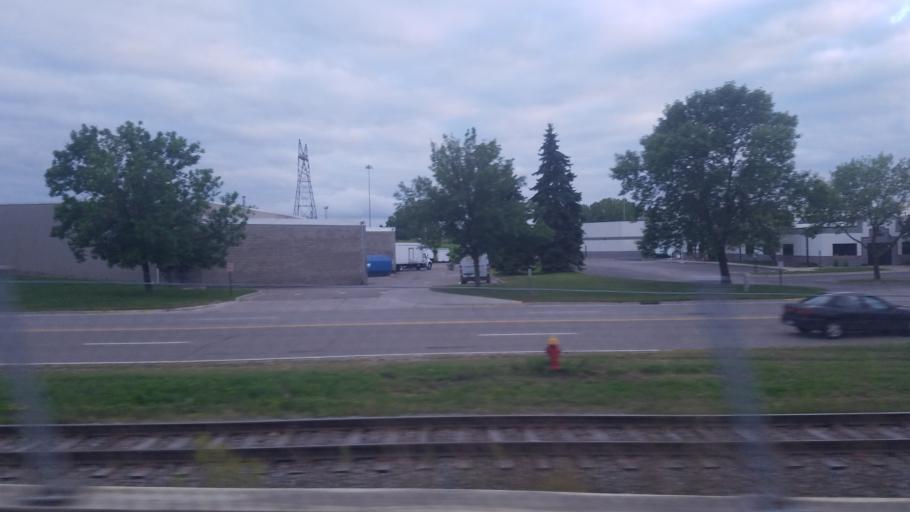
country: US
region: Minnesota
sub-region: Ramsey County
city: Falcon Heights
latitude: 44.9740
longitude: -93.1854
